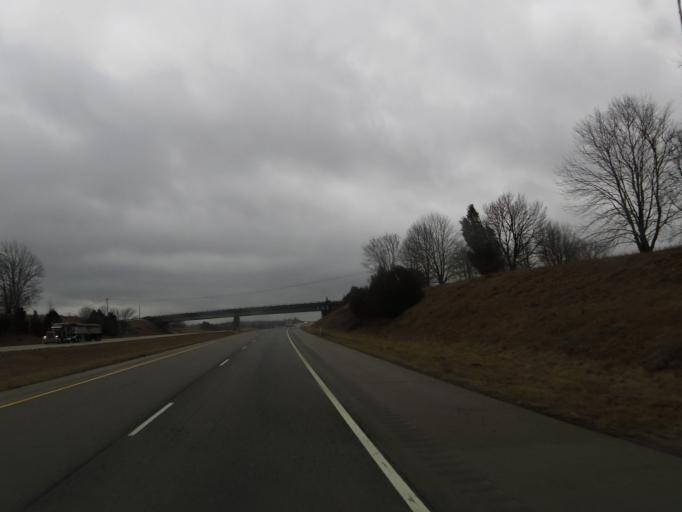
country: US
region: Illinois
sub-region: Johnson County
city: Goreville
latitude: 37.5812
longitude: -88.9657
